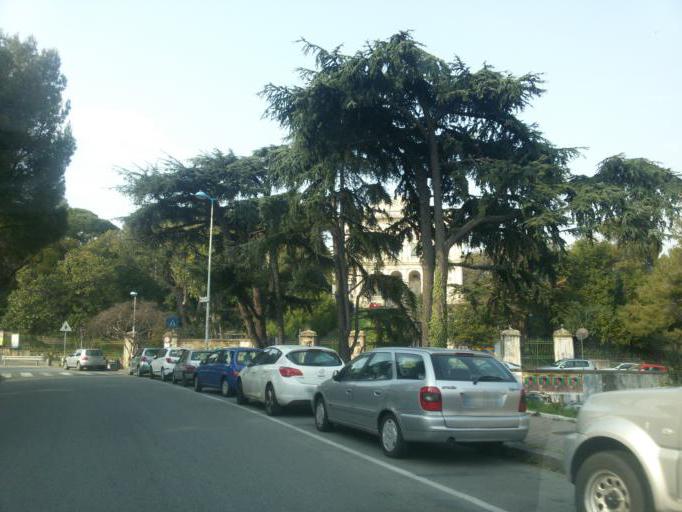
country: IT
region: Liguria
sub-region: Provincia di Genova
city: Genoa
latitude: 44.3987
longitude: 8.9627
